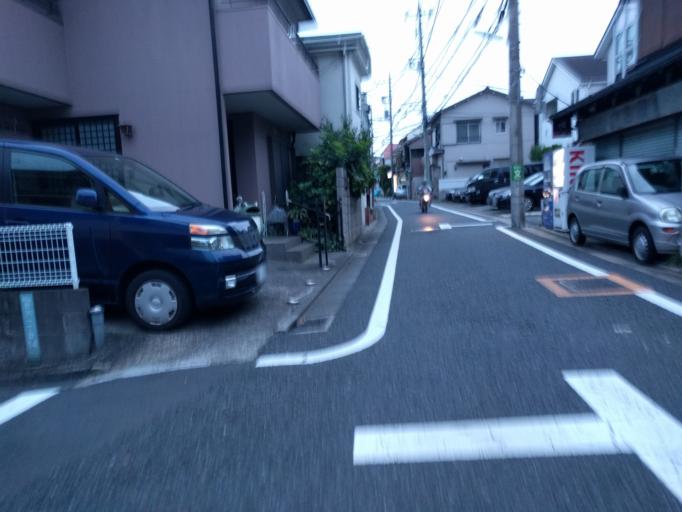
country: JP
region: Tokyo
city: Tokyo
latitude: 35.6365
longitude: 139.6688
